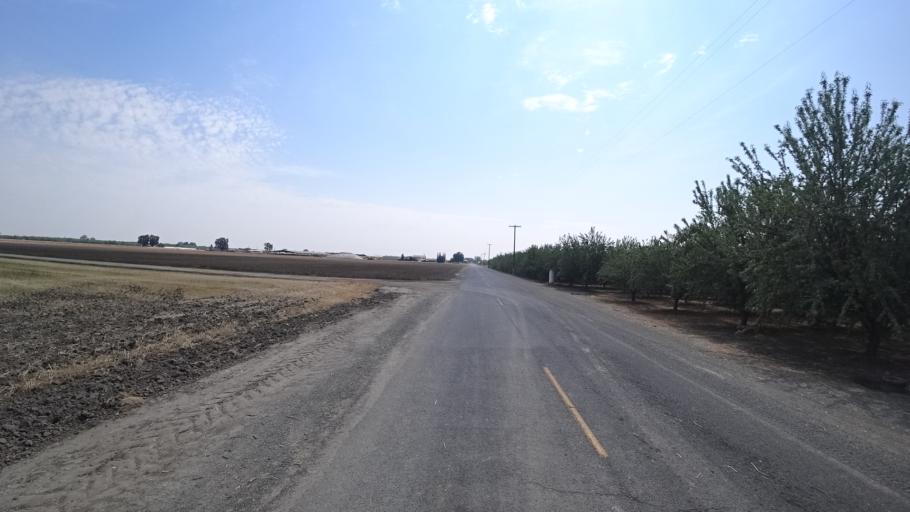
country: US
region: California
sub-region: Fresno County
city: Riverdale
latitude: 36.3948
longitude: -119.7873
